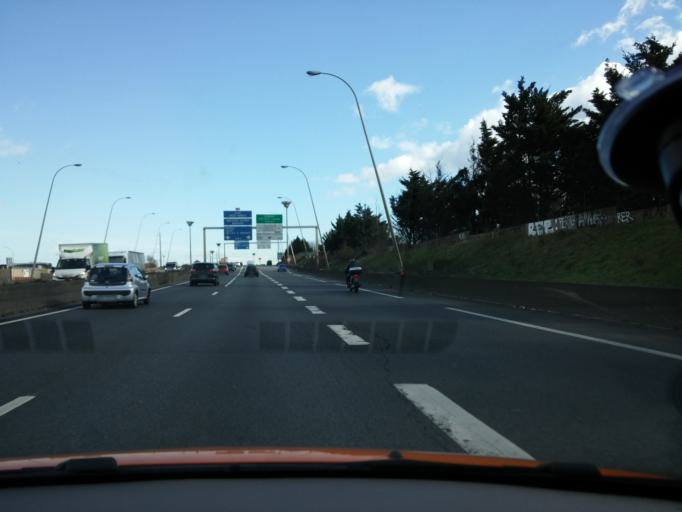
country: FR
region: Ile-de-France
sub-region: Departement du Val-de-Marne
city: Choisy-le-Roi
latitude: 48.7760
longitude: 2.4275
